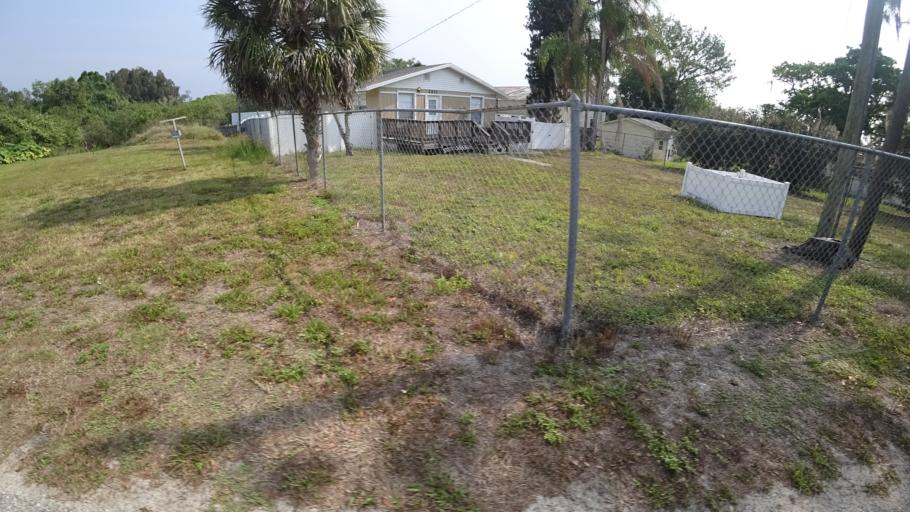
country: US
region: Florida
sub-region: Manatee County
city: Samoset
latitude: 27.4755
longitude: -82.4982
